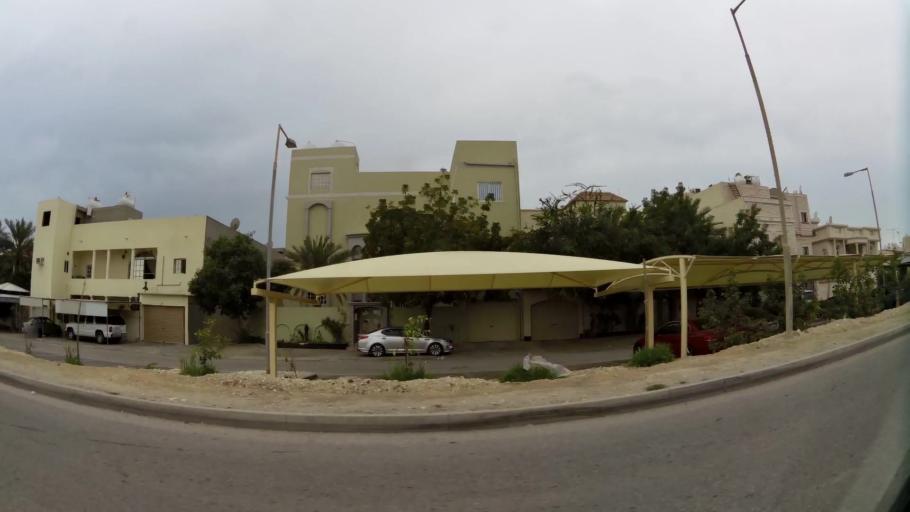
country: BH
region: Central Governorate
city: Madinat Hamad
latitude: 26.1131
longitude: 50.4989
